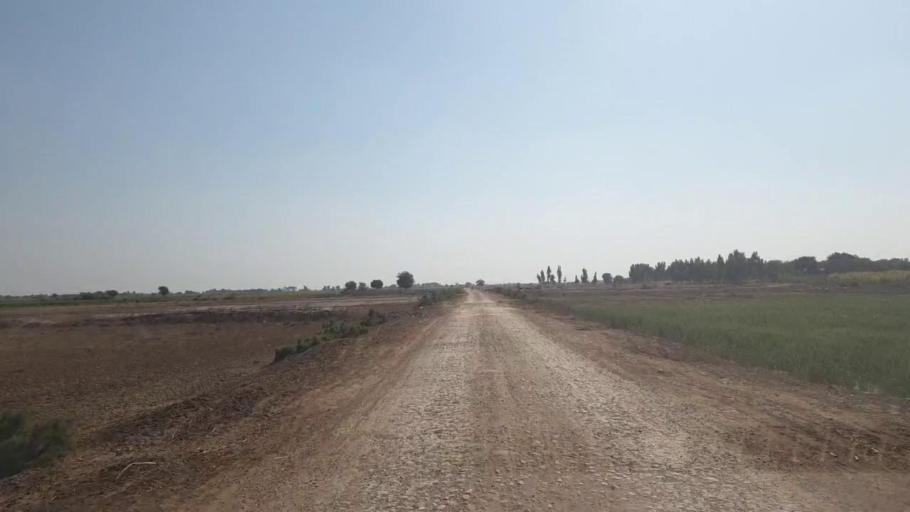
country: PK
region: Sindh
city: Chambar
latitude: 25.3051
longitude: 68.7418
